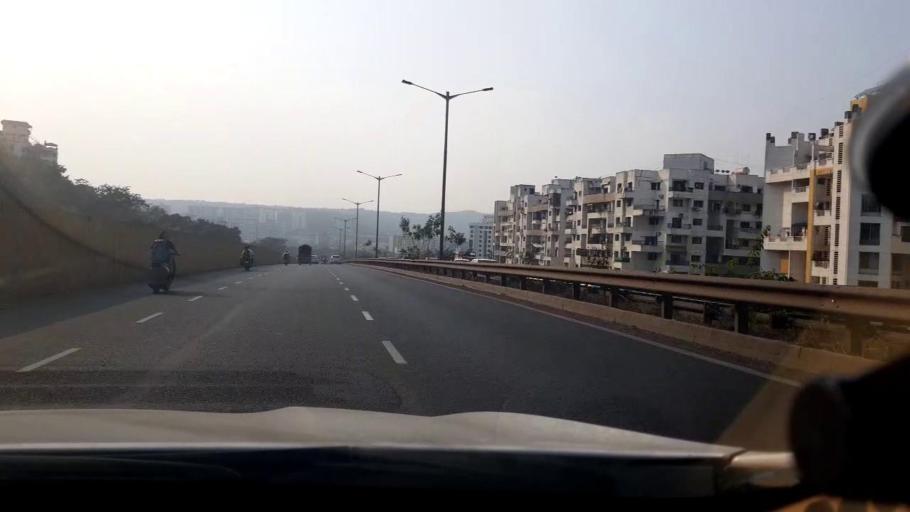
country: IN
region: Maharashtra
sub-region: Pune Division
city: Kharakvasla
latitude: 18.5085
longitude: 73.7784
